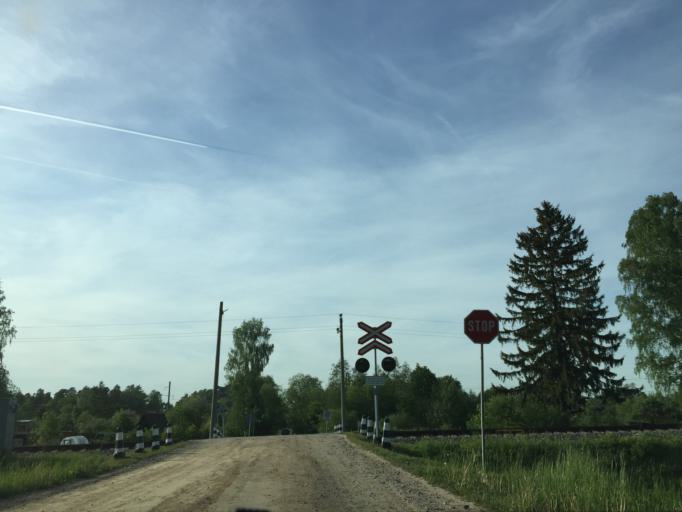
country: LV
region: Jelgava
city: Jelgava
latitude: 56.6284
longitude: 23.6851
